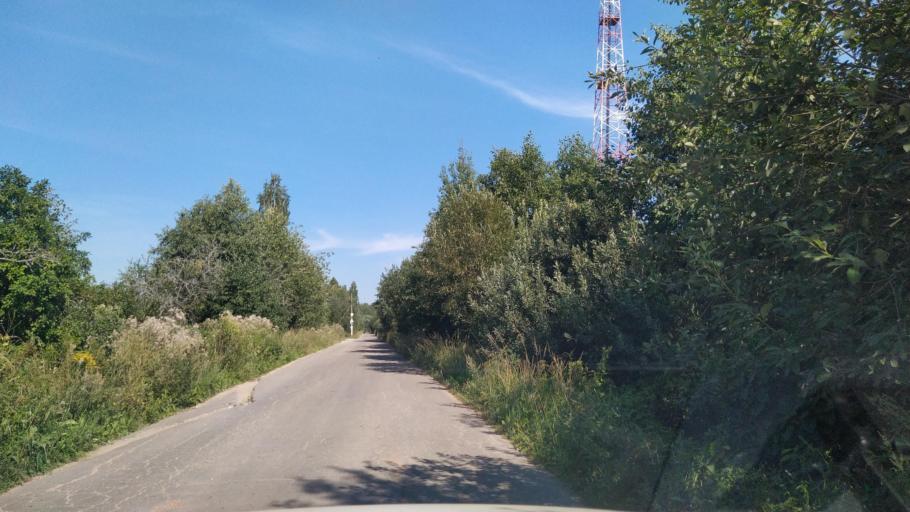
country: RU
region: Leningrad
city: Siverskiy
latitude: 59.2862
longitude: 30.0302
